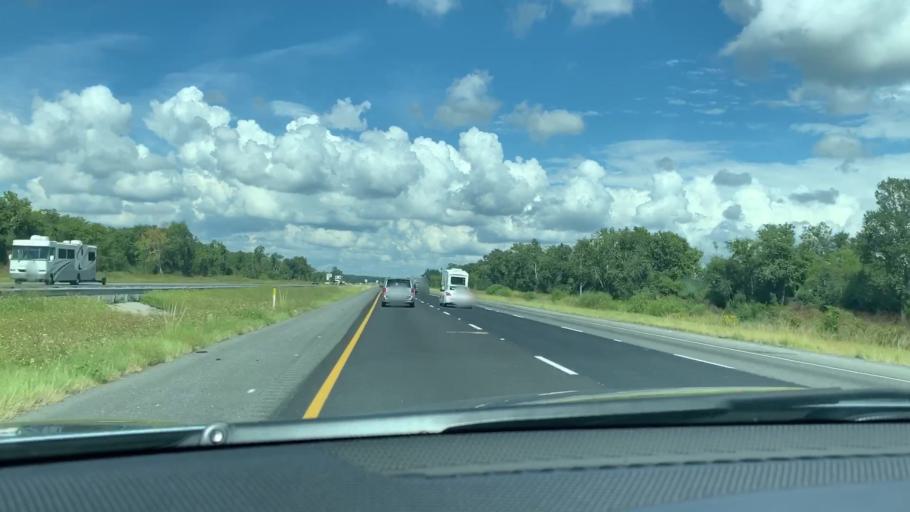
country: US
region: Georgia
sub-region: Camden County
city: Woodbine
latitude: 31.0204
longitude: -81.6578
